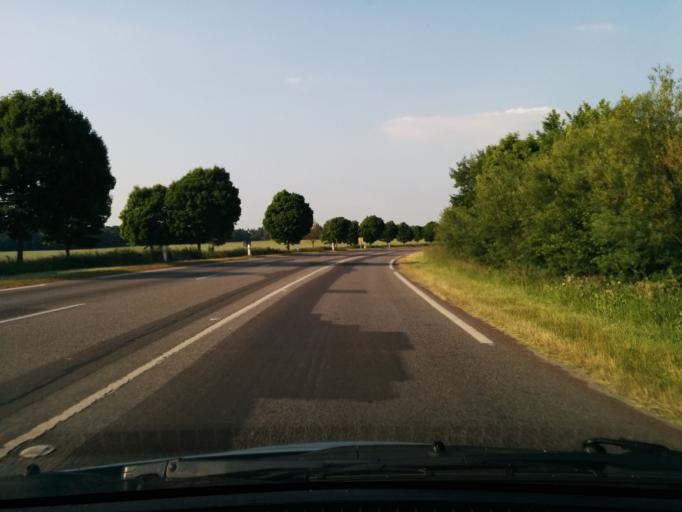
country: FR
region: Haute-Normandie
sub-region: Departement de l'Eure
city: Saint-Marcel
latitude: 49.0697
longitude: 1.4262
